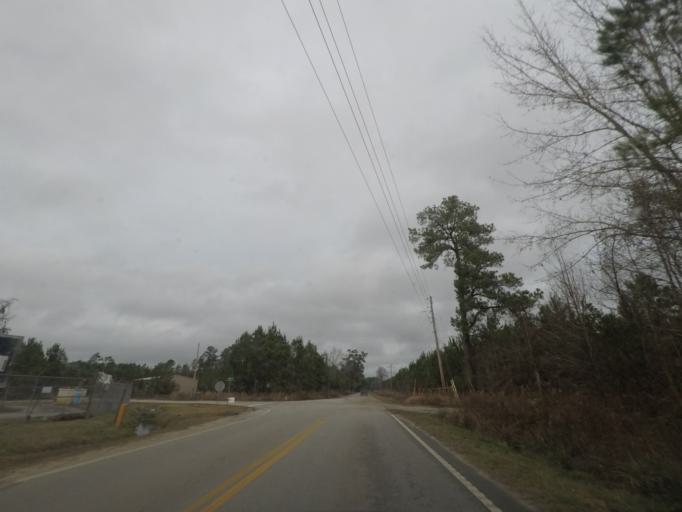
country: US
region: South Carolina
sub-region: Colleton County
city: Walterboro
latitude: 32.8726
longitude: -80.4887
